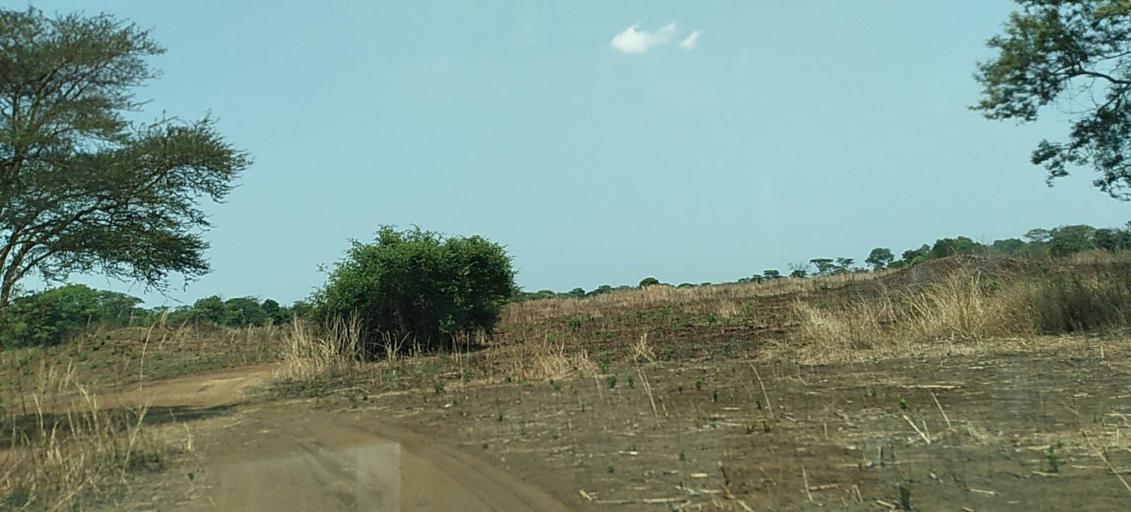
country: ZM
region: Copperbelt
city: Mpongwe
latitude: -13.8385
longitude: 27.8442
